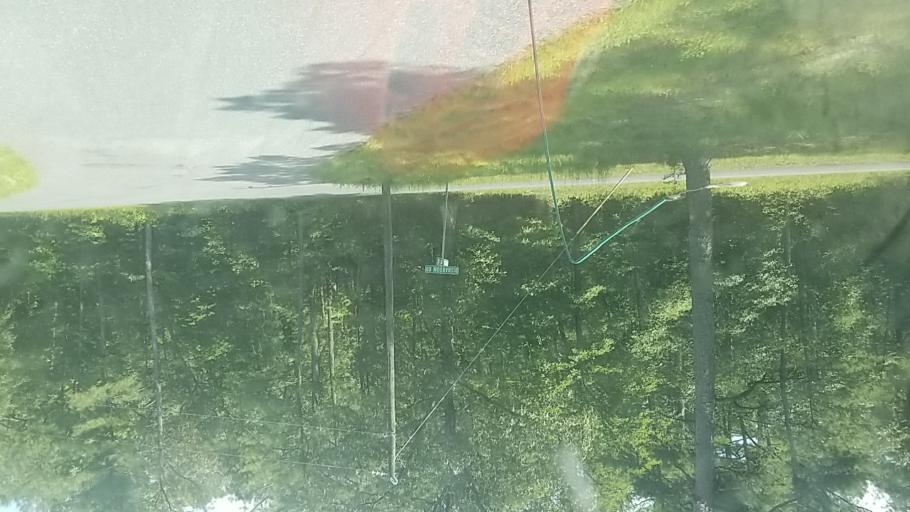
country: US
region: Maryland
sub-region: Worcester County
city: Snow Hill
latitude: 38.2503
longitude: -75.4325
